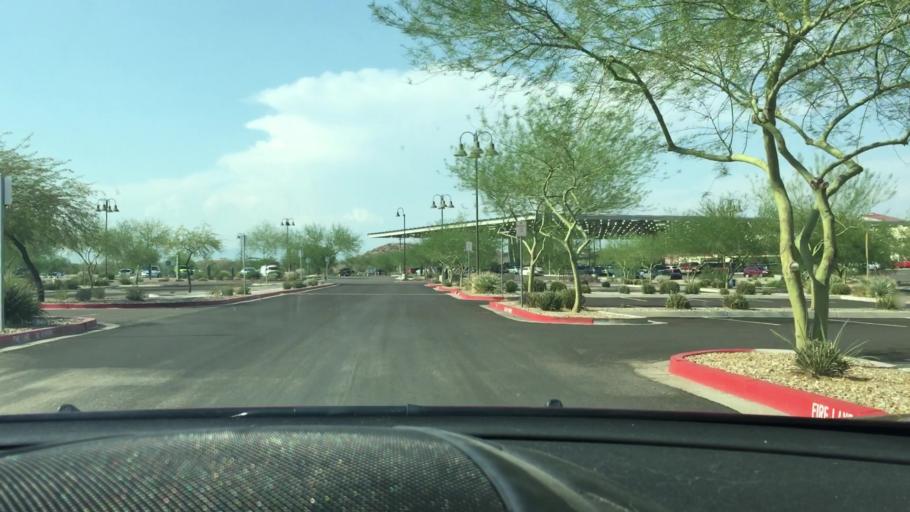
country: US
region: Arizona
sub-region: Maricopa County
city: Sun City West
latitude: 33.7124
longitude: -112.2697
